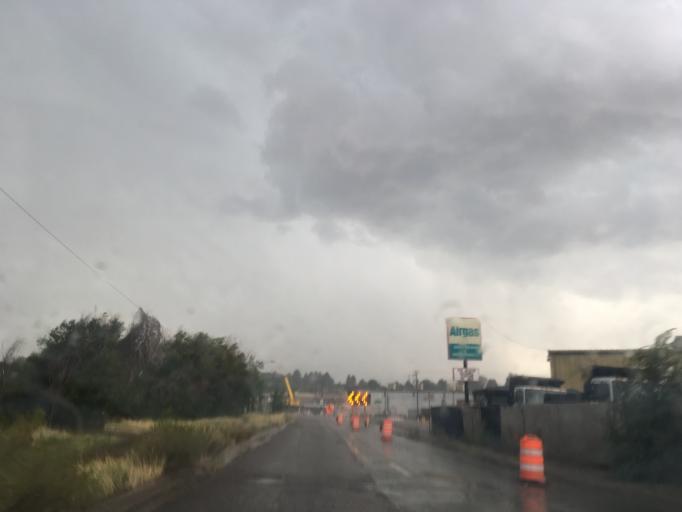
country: US
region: Colorado
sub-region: Arapahoe County
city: Englewood
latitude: 39.6917
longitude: -104.9968
